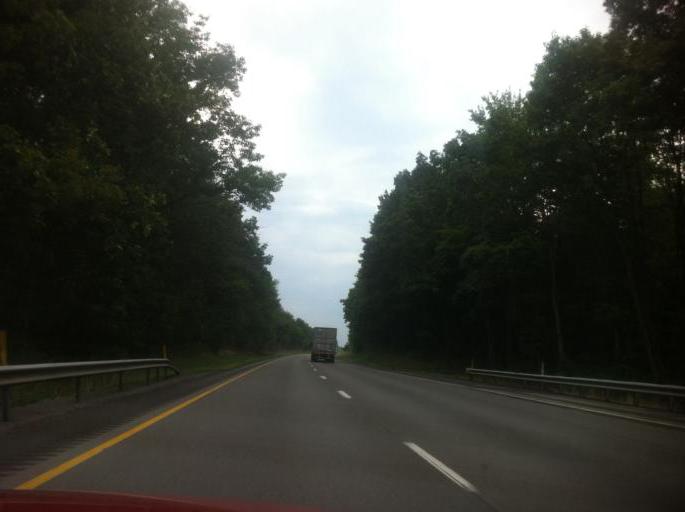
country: US
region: Pennsylvania
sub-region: Jefferson County
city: Brookville
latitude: 41.1719
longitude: -79.1044
